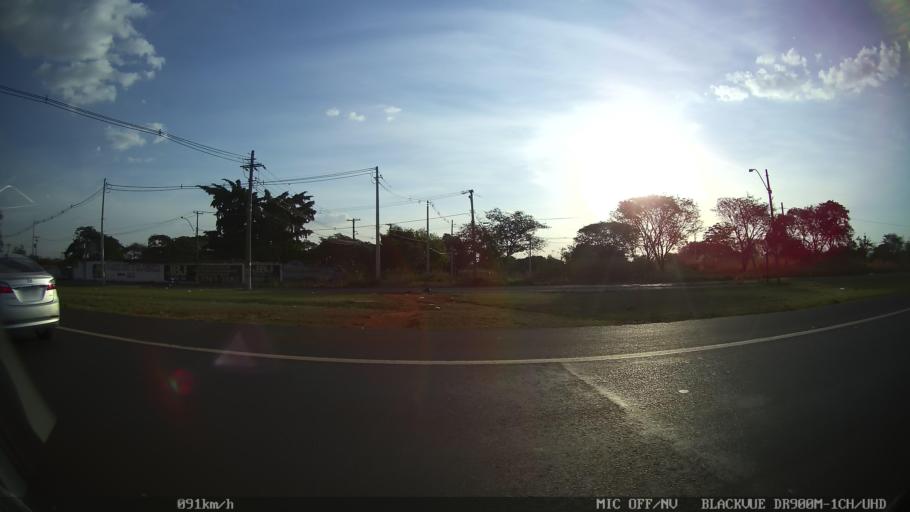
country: BR
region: Sao Paulo
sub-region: Ribeirao Preto
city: Ribeirao Preto
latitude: -21.1203
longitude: -47.7861
